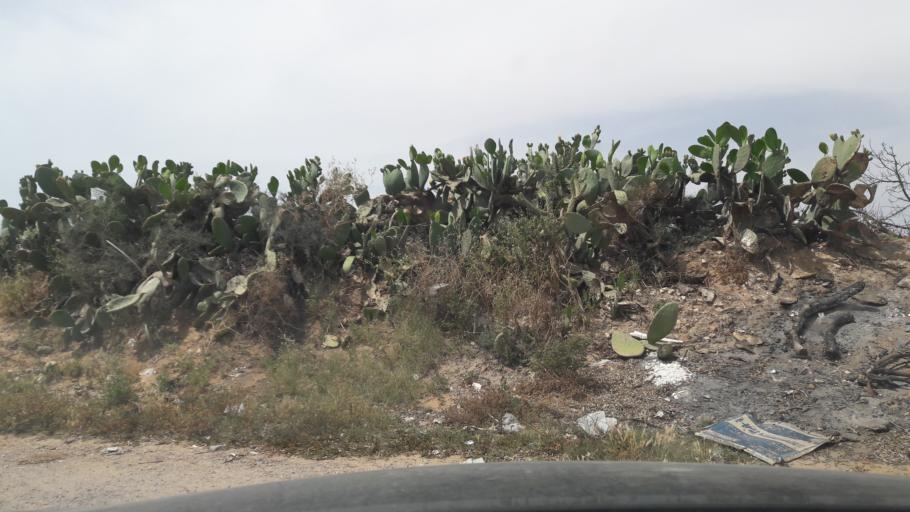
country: TN
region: Safaqis
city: Sfax
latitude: 34.7854
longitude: 10.7539
